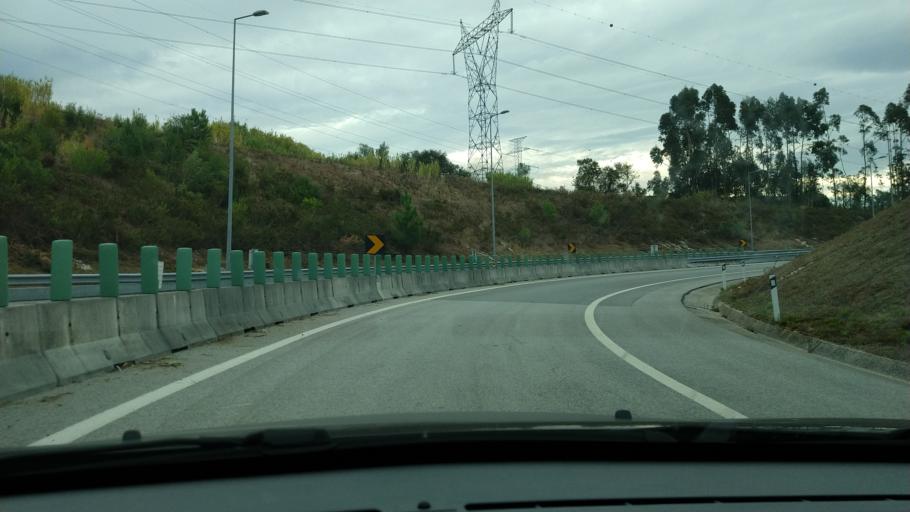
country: PT
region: Coimbra
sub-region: Figueira da Foz
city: Alhadas
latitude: 40.1593
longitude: -8.7747
